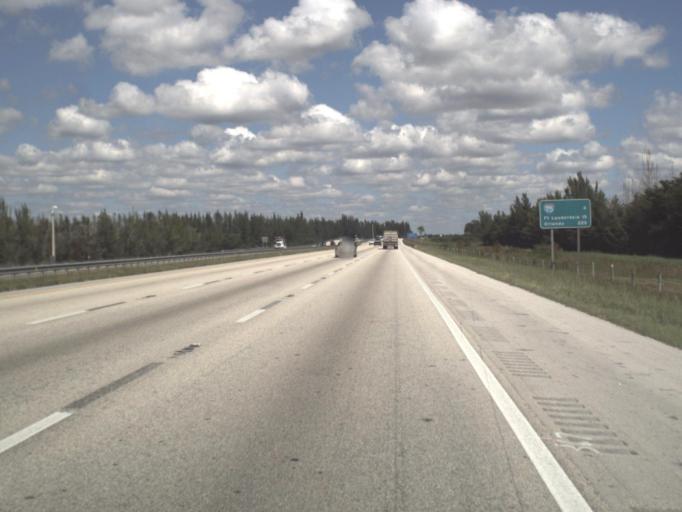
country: US
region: Florida
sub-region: Miami-Dade County
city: Palm Springs North
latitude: 25.9219
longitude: -80.3775
